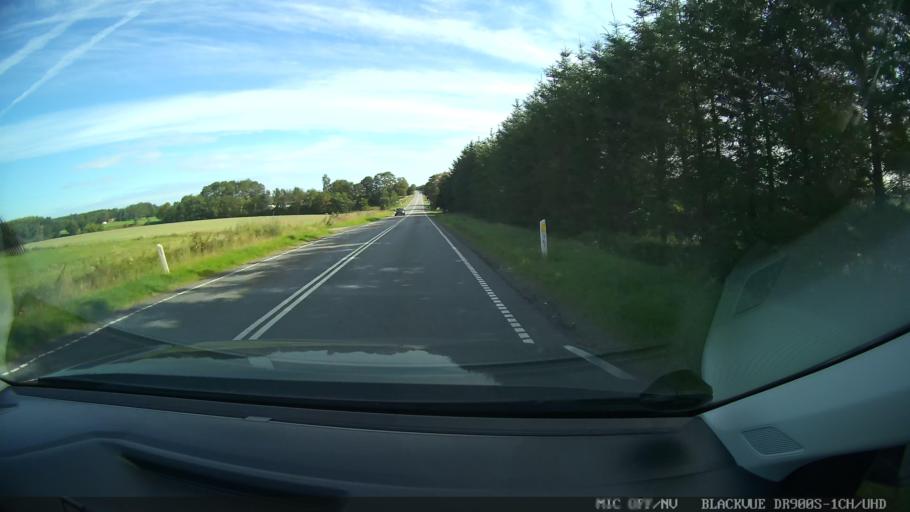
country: DK
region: North Denmark
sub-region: Rebild Kommune
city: Skorping
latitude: 56.7755
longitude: 10.0037
